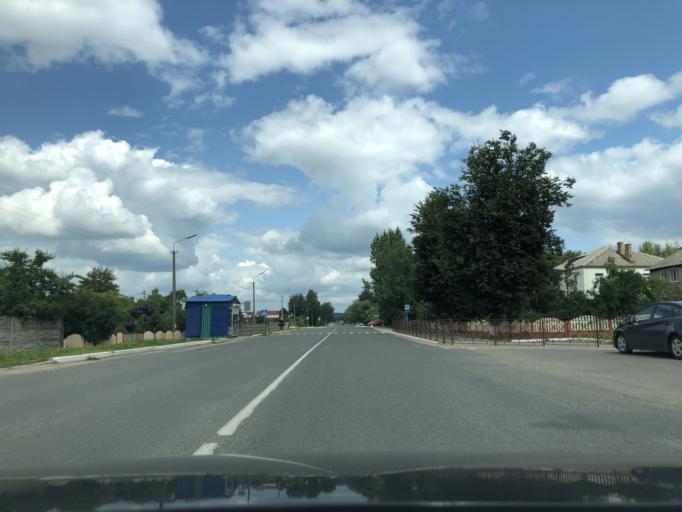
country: BY
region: Minsk
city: Lahoysk
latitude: 54.2106
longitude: 27.8518
